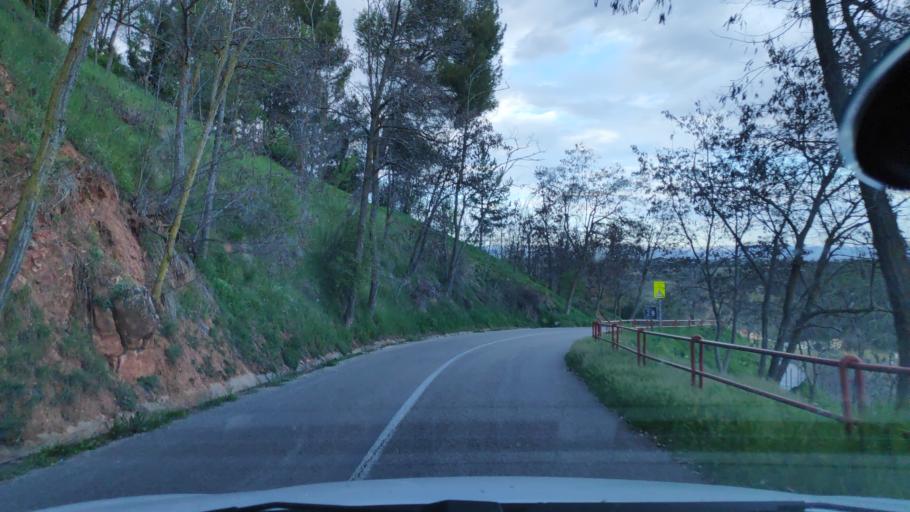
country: ES
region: Castille and Leon
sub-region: Provincia de Soria
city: Soria
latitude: 41.7620
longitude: -2.4571
